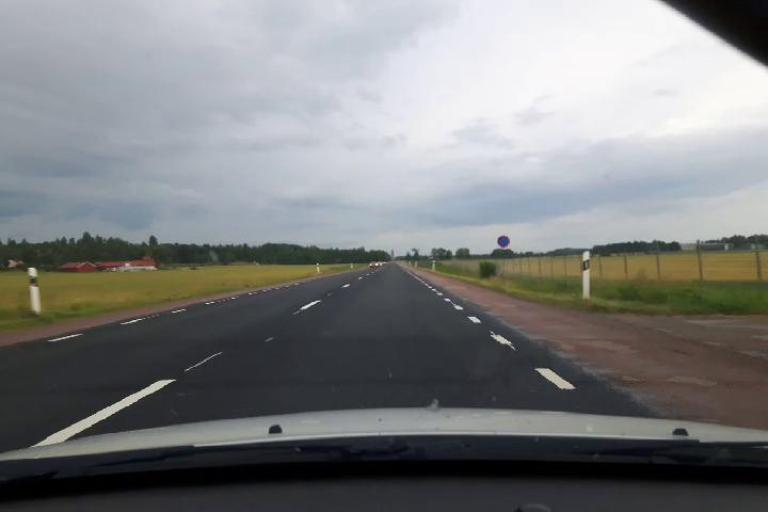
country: SE
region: Uppsala
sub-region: Uppsala Kommun
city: Gamla Uppsala
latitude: 59.8944
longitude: 17.6152
